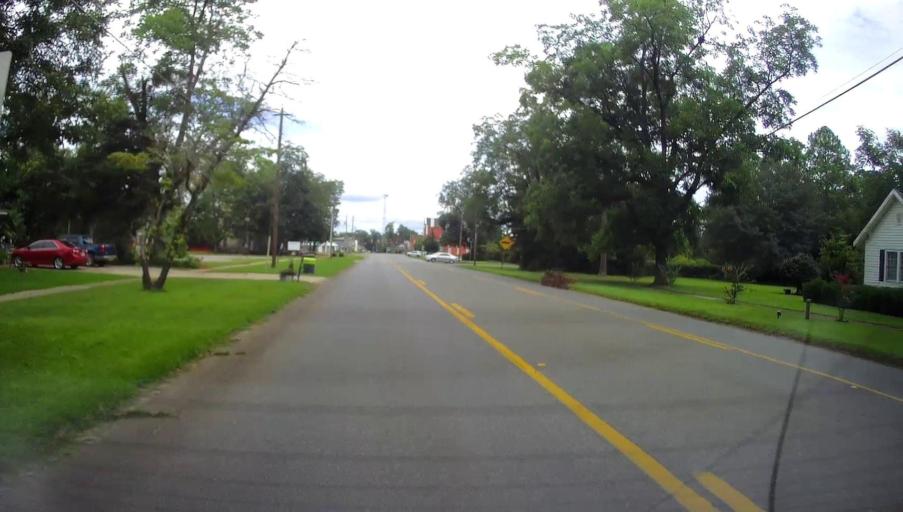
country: US
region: Georgia
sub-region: Schley County
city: Ellaville
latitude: 32.2382
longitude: -84.3114
